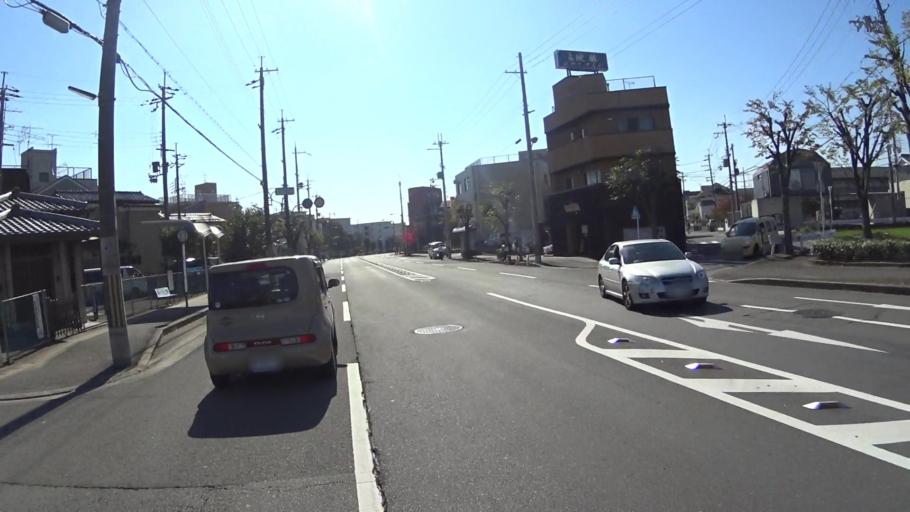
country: JP
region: Kyoto
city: Muko
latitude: 34.9323
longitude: 135.6879
